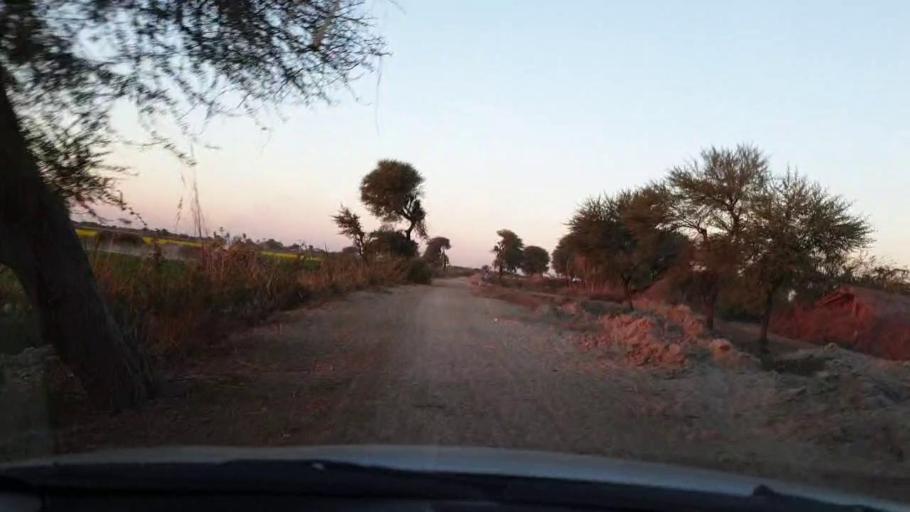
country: PK
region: Sindh
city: Jhol
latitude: 25.9107
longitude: 68.8854
